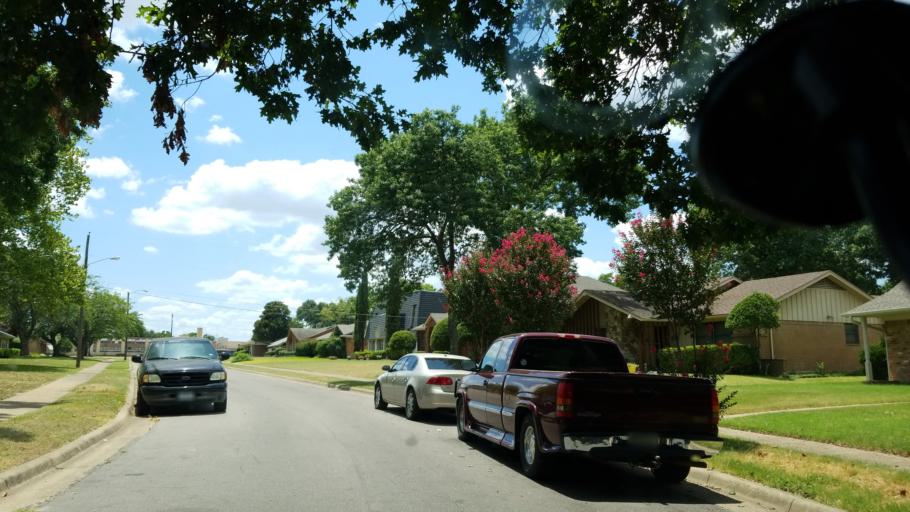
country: US
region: Texas
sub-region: Dallas County
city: Cockrell Hill
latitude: 32.6981
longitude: -96.8523
